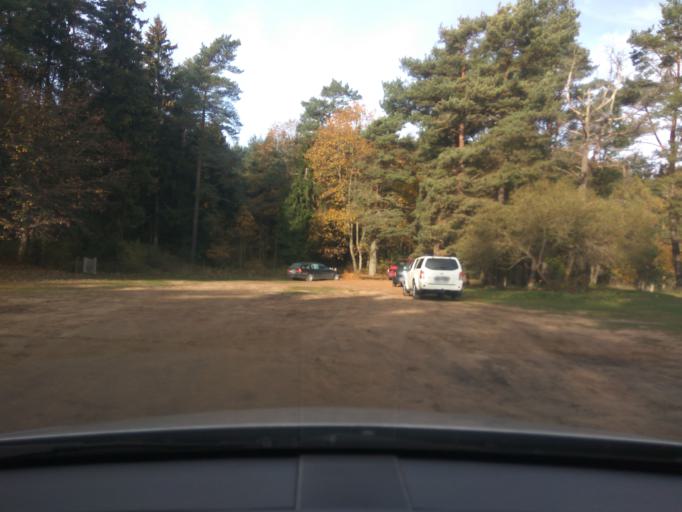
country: LV
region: Alsunga
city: Alsunga
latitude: 57.0054
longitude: 21.3816
